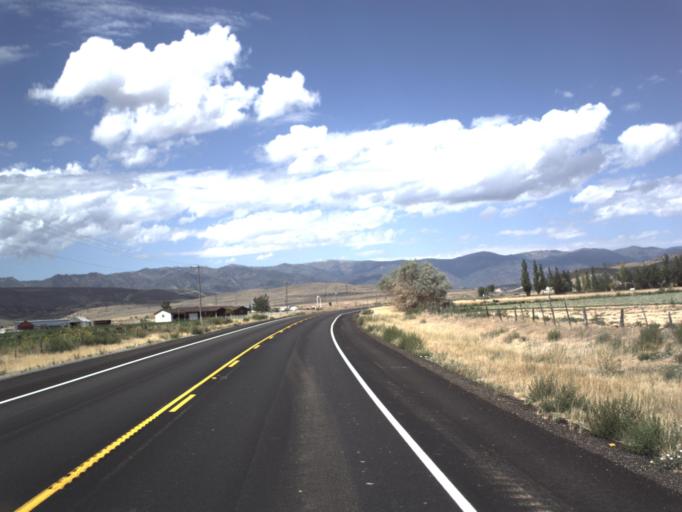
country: US
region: Utah
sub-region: Sevier County
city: Aurora
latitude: 38.9551
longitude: -111.9115
